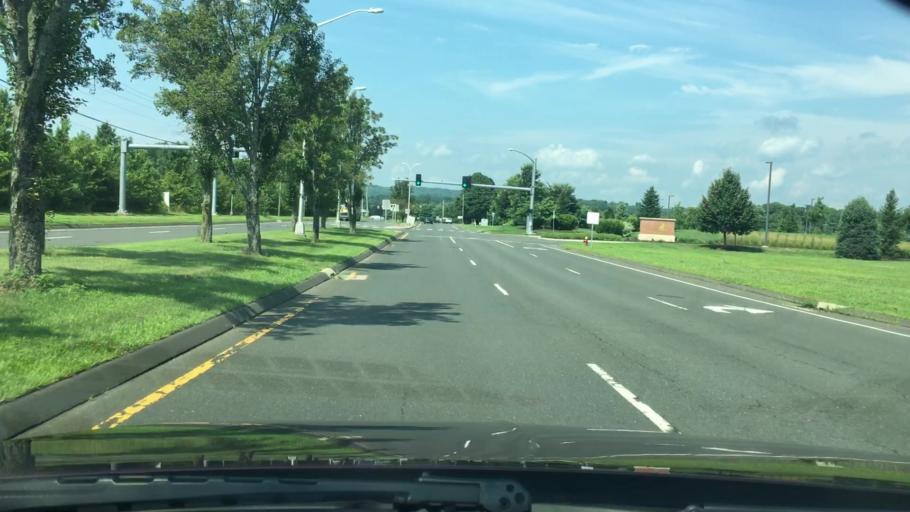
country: US
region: Connecticut
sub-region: Hartford County
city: Tariffville
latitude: 41.8762
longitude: -72.7260
